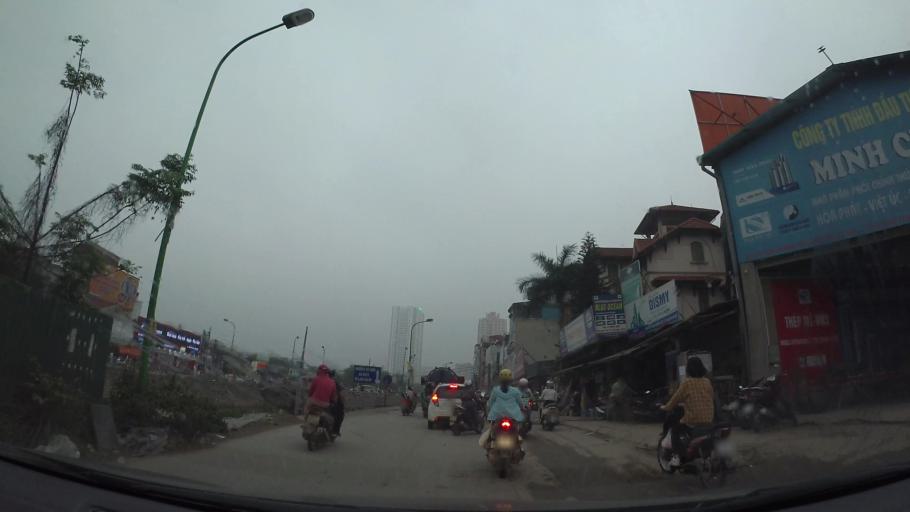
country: VN
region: Ha Noi
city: Hai BaTrung
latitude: 20.9835
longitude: 105.8345
